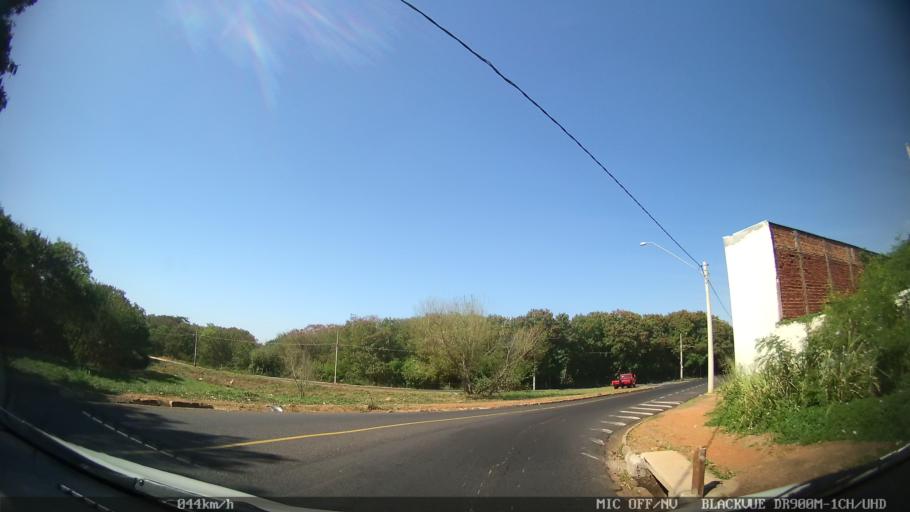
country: BR
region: Sao Paulo
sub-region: Sao Jose Do Rio Preto
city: Sao Jose do Rio Preto
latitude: -20.7792
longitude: -49.3840
